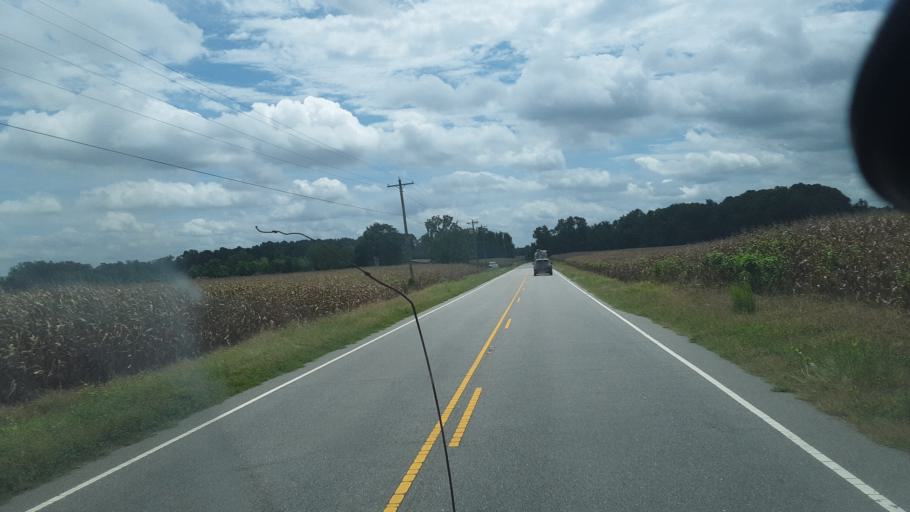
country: US
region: North Carolina
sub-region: Robeson County
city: Rowland
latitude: 34.4980
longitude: -79.2561
